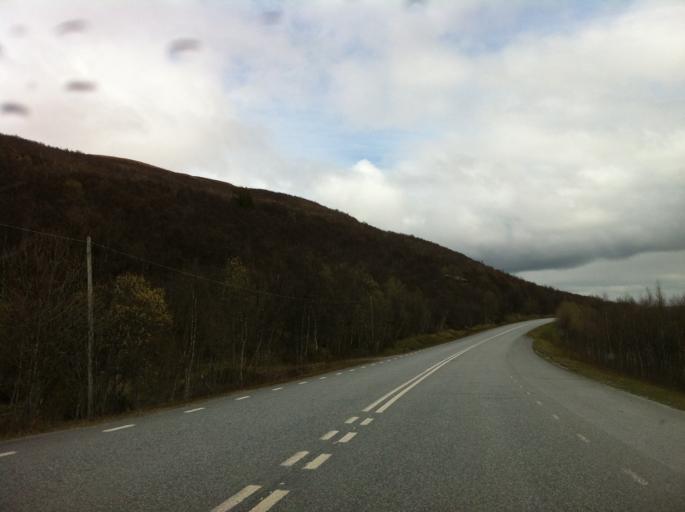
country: NO
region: Sor-Trondelag
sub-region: Tydal
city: Aas
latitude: 62.5697
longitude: 12.2402
